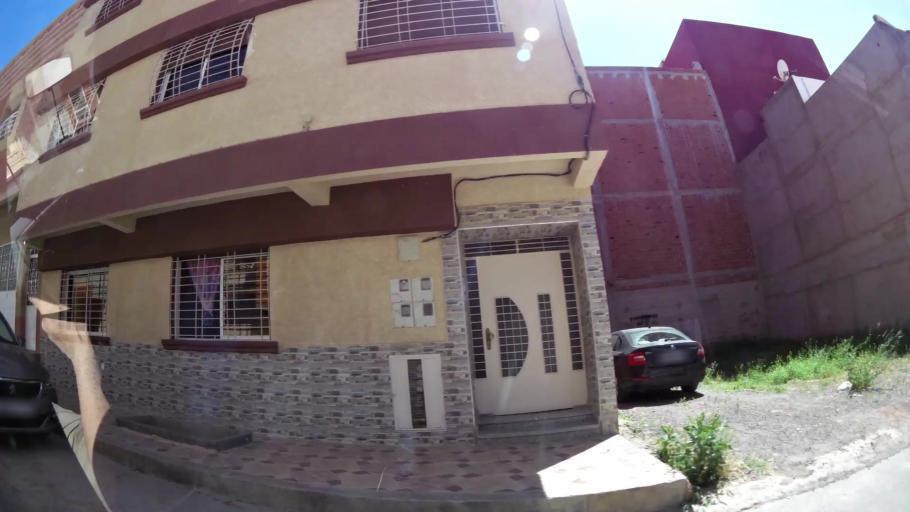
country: MA
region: Oriental
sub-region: Oujda-Angad
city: Oujda
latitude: 34.6473
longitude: -1.9090
